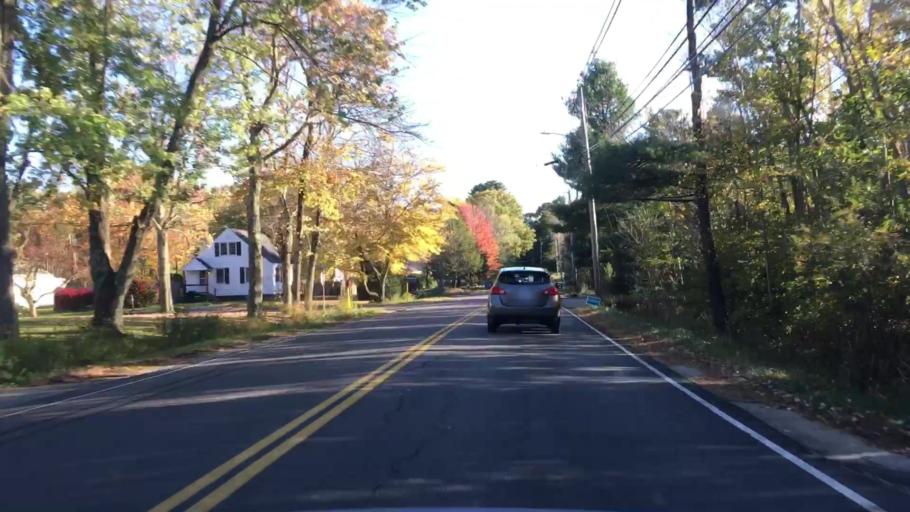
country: US
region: Maine
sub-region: Cumberland County
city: Scarborough
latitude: 43.6082
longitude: -70.3392
